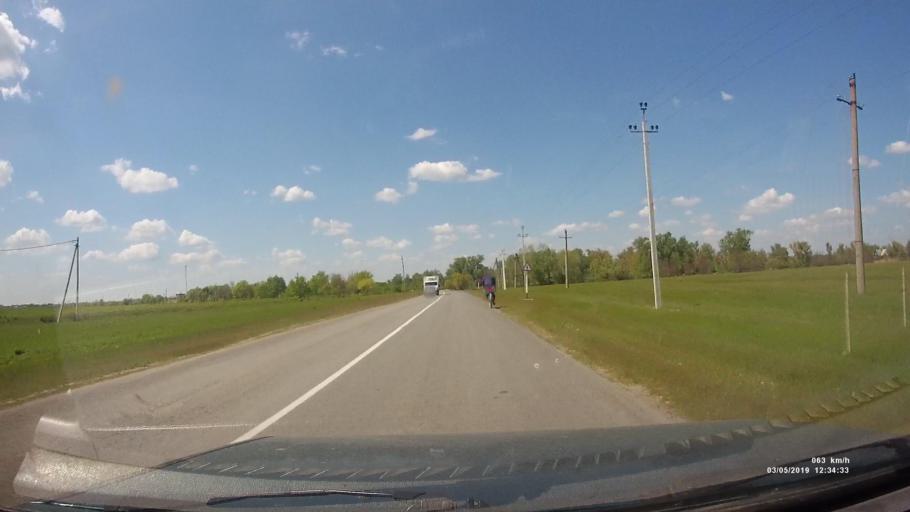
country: RU
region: Rostov
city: Semikarakorsk
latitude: 47.5220
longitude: 40.7685
